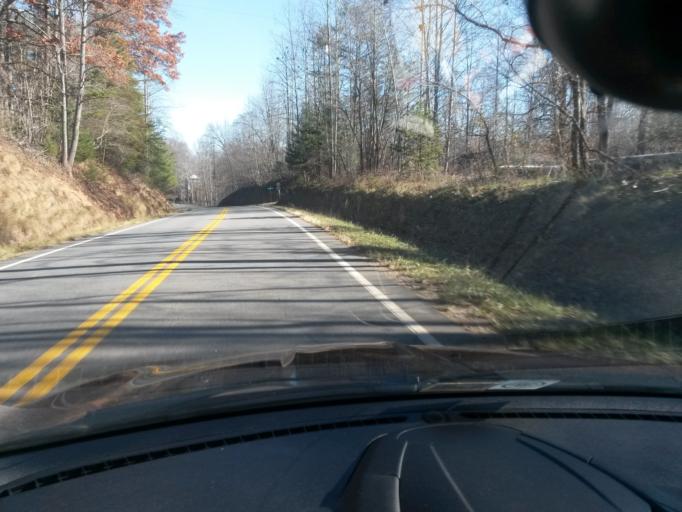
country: US
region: Virginia
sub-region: Henry County
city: Pannill Fork
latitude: 36.7760
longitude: -80.1372
